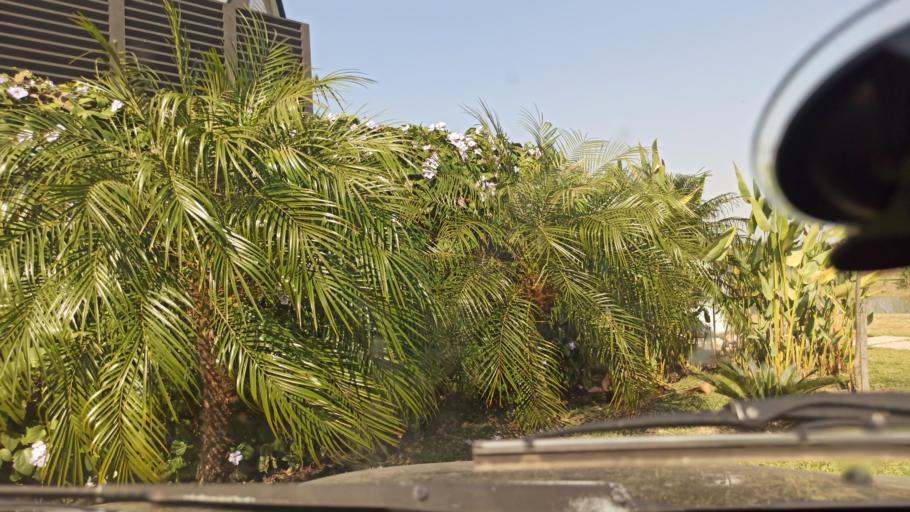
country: PY
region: Central
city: Colonia Mariano Roque Alonso
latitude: -25.1971
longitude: -57.5688
